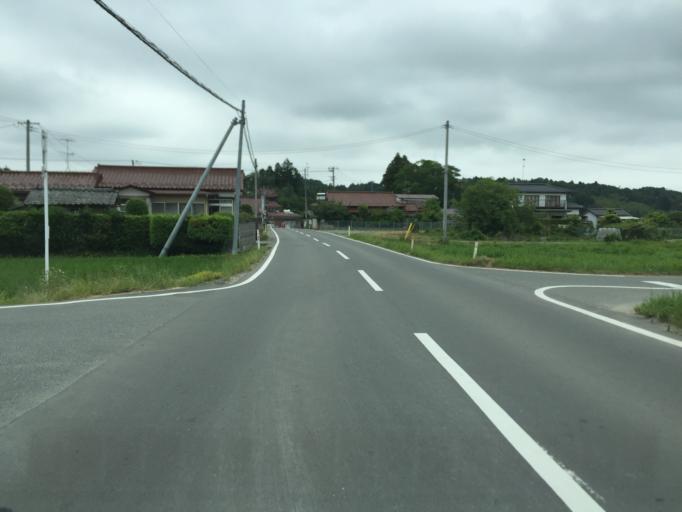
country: JP
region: Miyagi
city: Marumori
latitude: 37.7513
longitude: 140.9155
